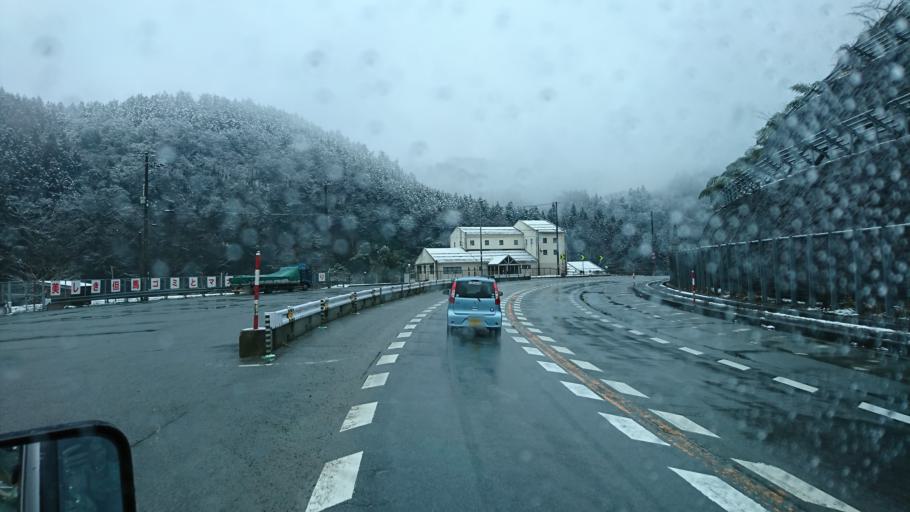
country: JP
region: Hyogo
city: Toyooka
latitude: 35.4776
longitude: 134.5853
